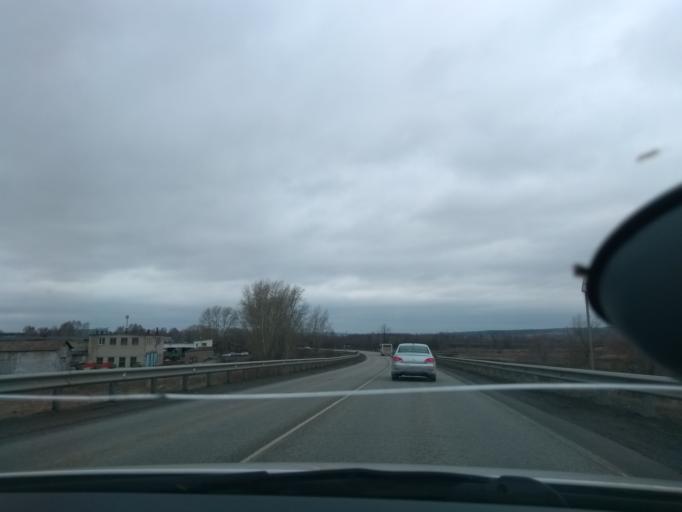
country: RU
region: Perm
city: Kungur
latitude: 57.4497
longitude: 56.8091
